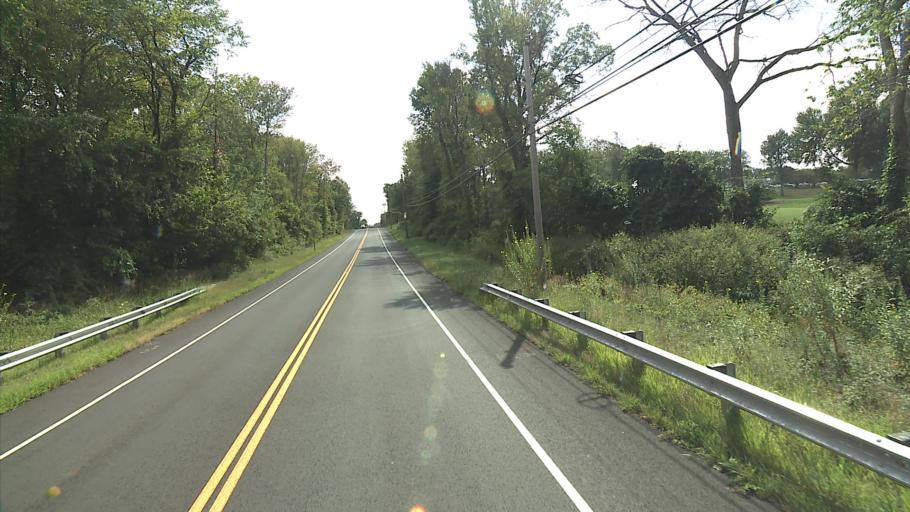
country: US
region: Connecticut
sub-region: Hartford County
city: Blue Hills
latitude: 41.7992
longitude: -72.7287
